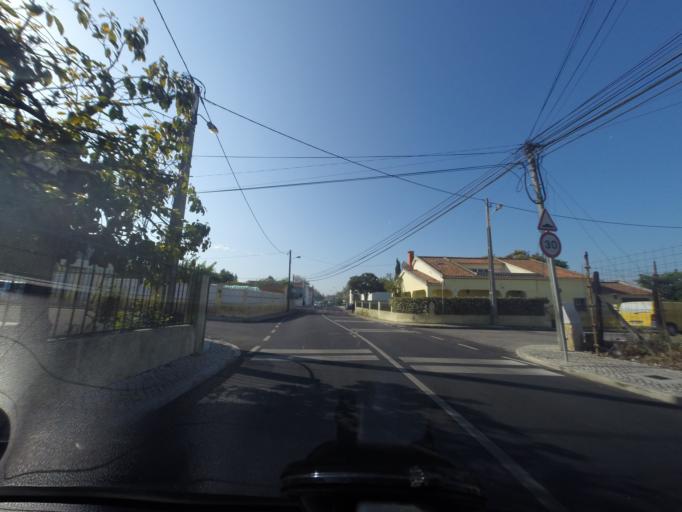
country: PT
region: Lisbon
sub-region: Cascais
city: Sao Domingos de Rana
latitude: 38.7199
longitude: -9.3430
